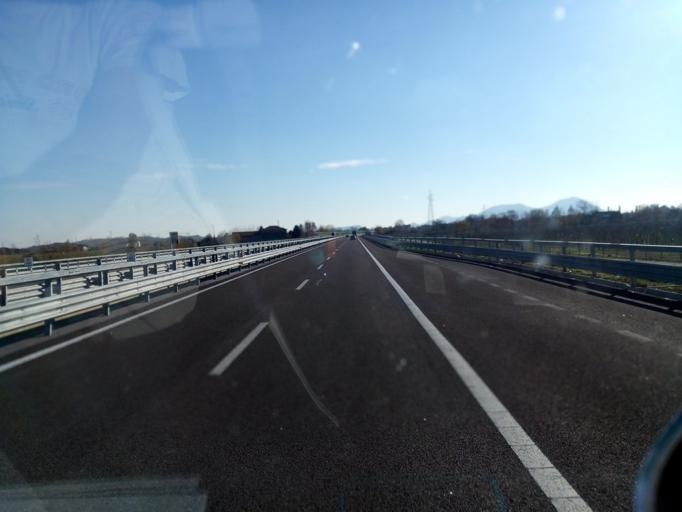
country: IT
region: Veneto
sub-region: Provincia di Vicenza
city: Longare
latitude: 45.4786
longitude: 11.6307
